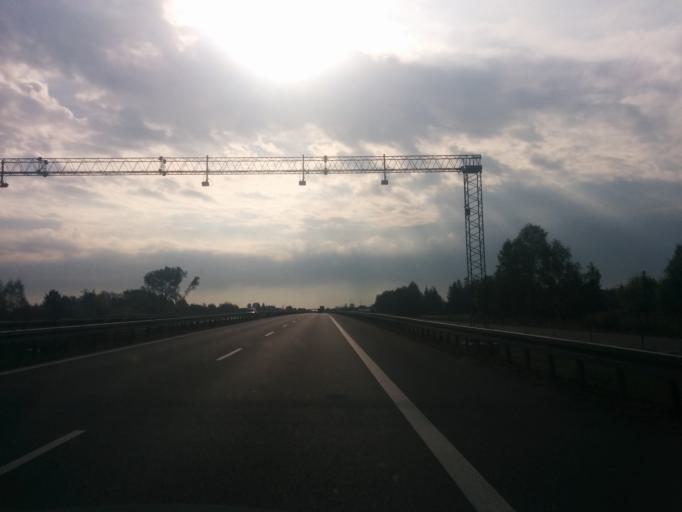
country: PL
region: Masovian Voivodeship
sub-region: Powiat bialobrzeski
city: Stara Blotnica
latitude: 51.5555
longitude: 21.0335
